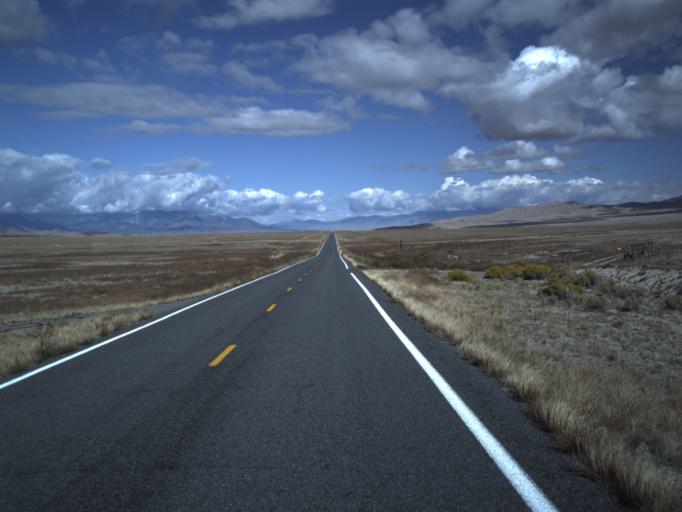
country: US
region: Utah
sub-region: Beaver County
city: Milford
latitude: 38.6334
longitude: -113.8559
